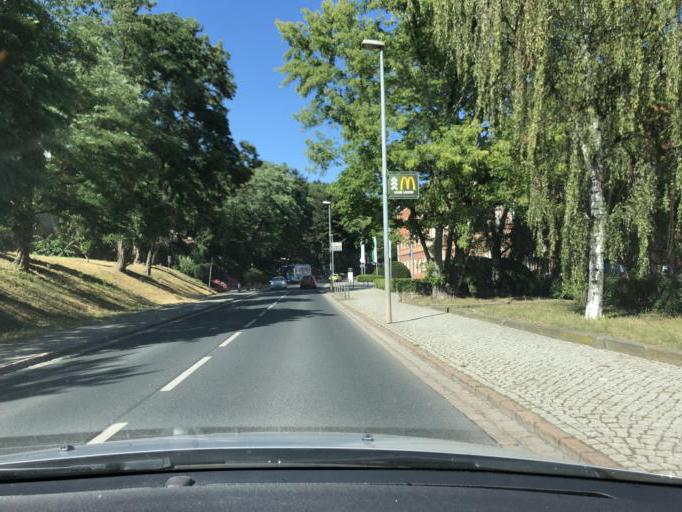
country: DE
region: Saxony
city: Meissen
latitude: 51.1558
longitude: 13.4635
